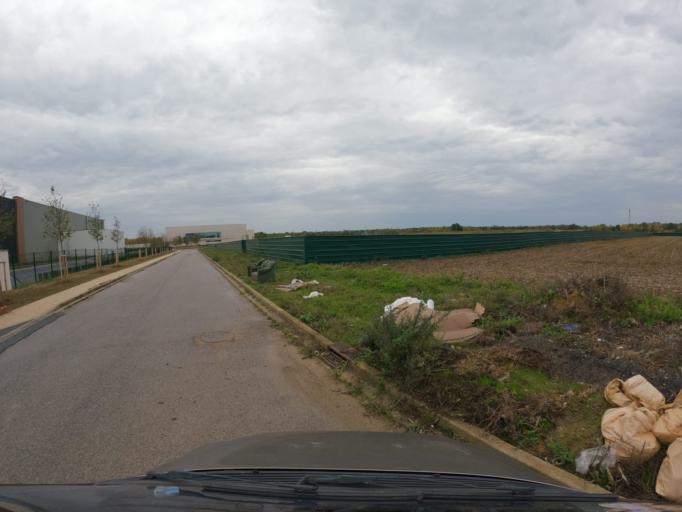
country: FR
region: Ile-de-France
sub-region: Departement de Seine-et-Marne
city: Serris
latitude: 48.8383
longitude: 2.8001
